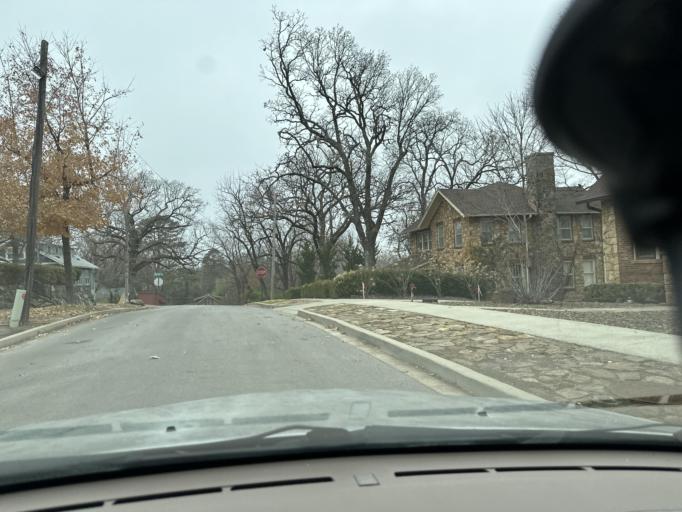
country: US
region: Arkansas
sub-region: Washington County
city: Fayetteville
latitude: 36.0713
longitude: -94.1595
